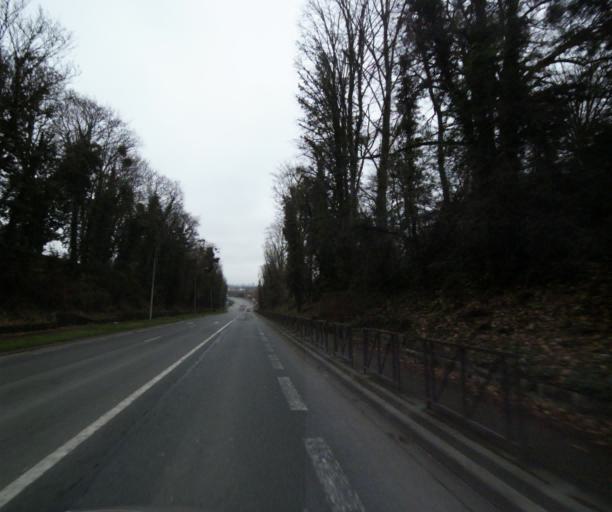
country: FR
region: Ile-de-France
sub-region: Departement du Val-de-Marne
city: Villeneuve-le-Roi
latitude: 48.7363
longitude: 2.4064
